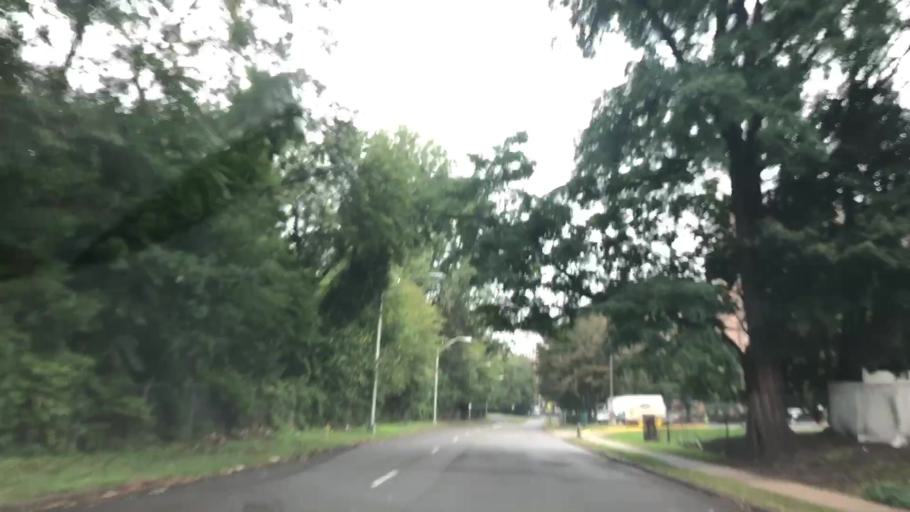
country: US
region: New Jersey
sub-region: Essex County
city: East Orange
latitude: 40.7765
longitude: -74.2010
